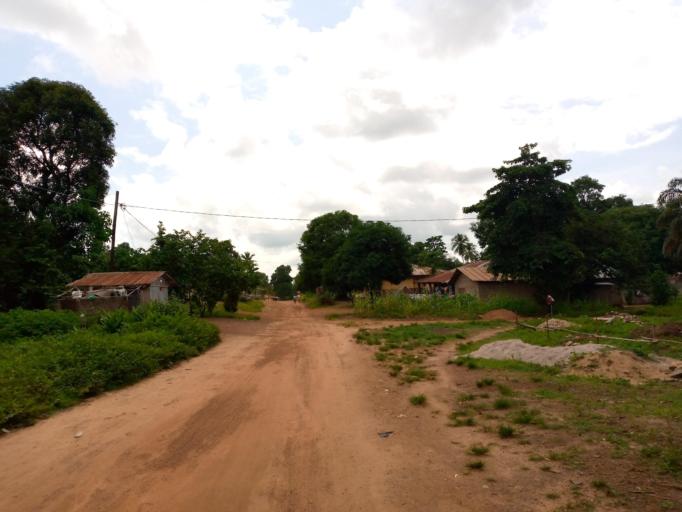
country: SL
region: Northern Province
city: Magburaka
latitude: 8.7114
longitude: -11.9341
